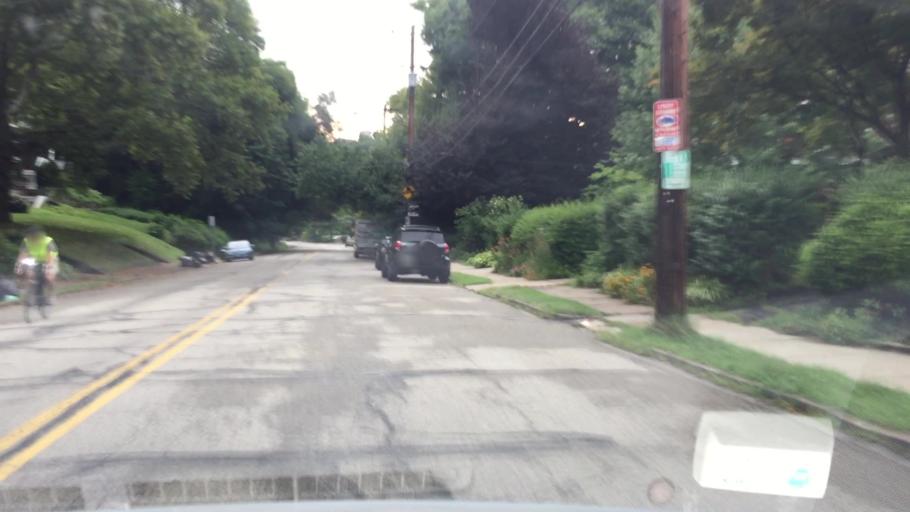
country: US
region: Pennsylvania
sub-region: Allegheny County
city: Bloomfield
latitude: 40.4455
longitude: -79.9335
